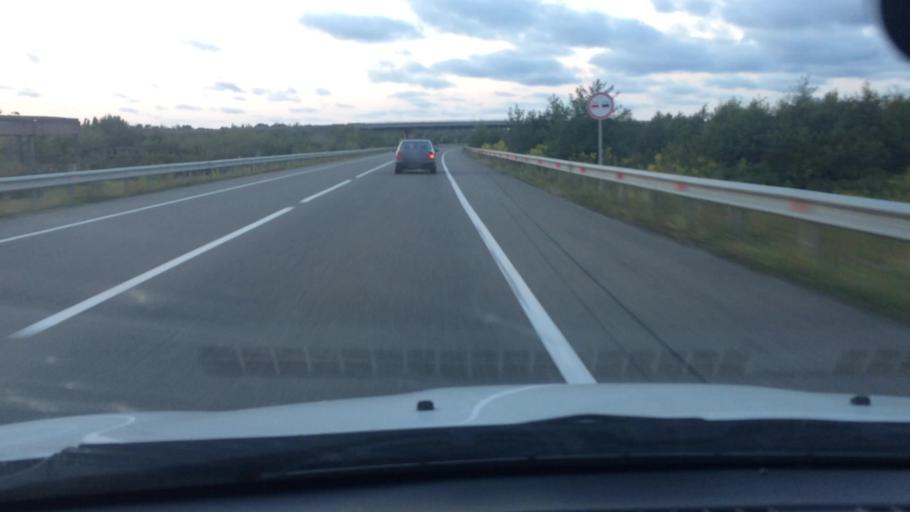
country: GE
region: Guria
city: Urek'i
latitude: 41.9157
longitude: 41.7775
